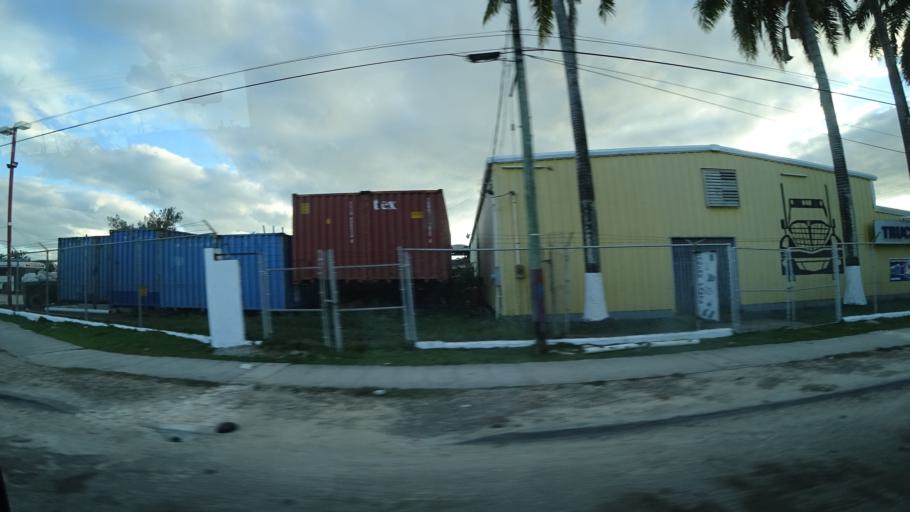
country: BZ
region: Belize
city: Belize City
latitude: 17.5092
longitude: -88.2081
